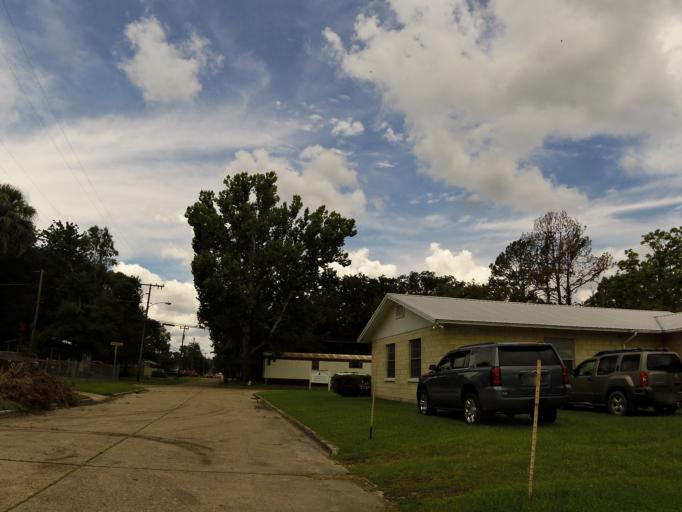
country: US
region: Florida
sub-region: Putnam County
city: East Palatka
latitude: 29.7183
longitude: -81.5049
